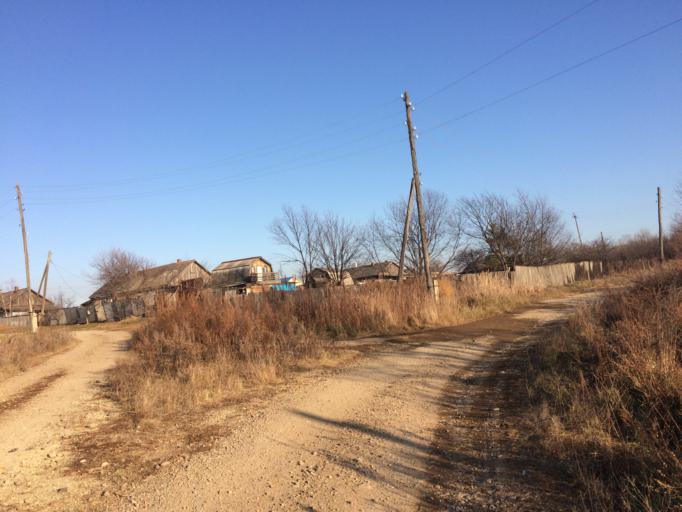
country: RU
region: Primorskiy
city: Ivanovka
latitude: 43.9555
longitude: 132.4675
